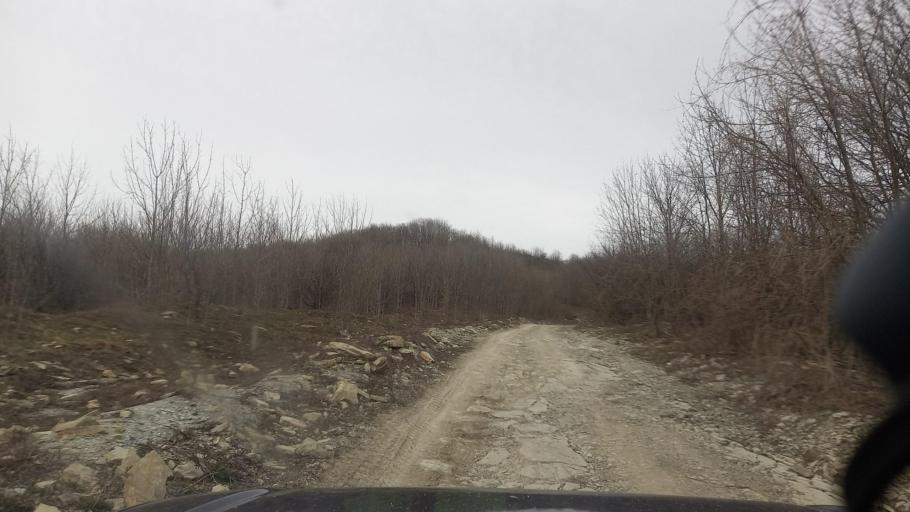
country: RU
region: Krasnodarskiy
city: Divnomorskoye
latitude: 44.6031
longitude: 38.2794
